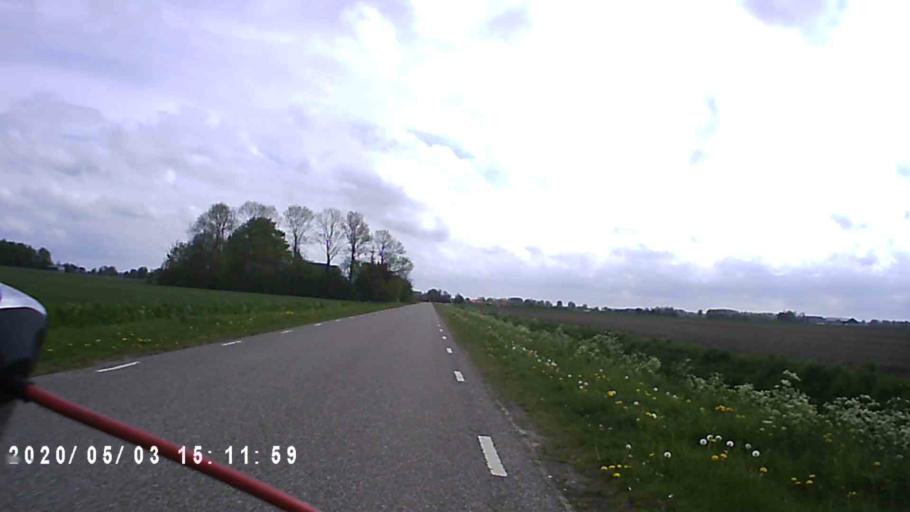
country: NL
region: Groningen
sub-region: Gemeente Winsum
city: Winsum
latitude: 53.3723
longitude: 6.4518
